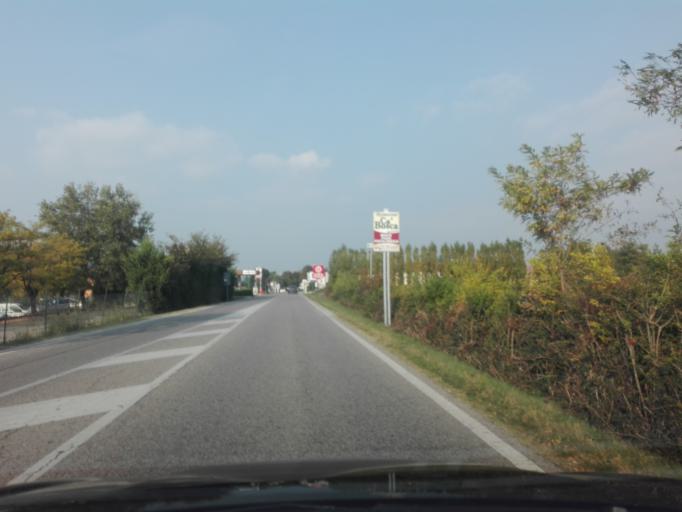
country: IT
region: Veneto
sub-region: Provincia di Verona
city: Cavalcaselle
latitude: 45.4594
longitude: 10.7168
